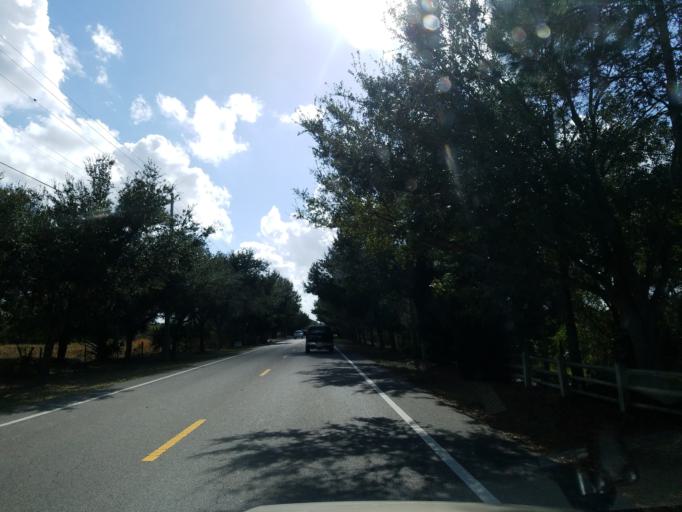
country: US
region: Florida
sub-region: Hillsborough County
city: Apollo Beach
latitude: 27.7892
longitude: -82.3679
